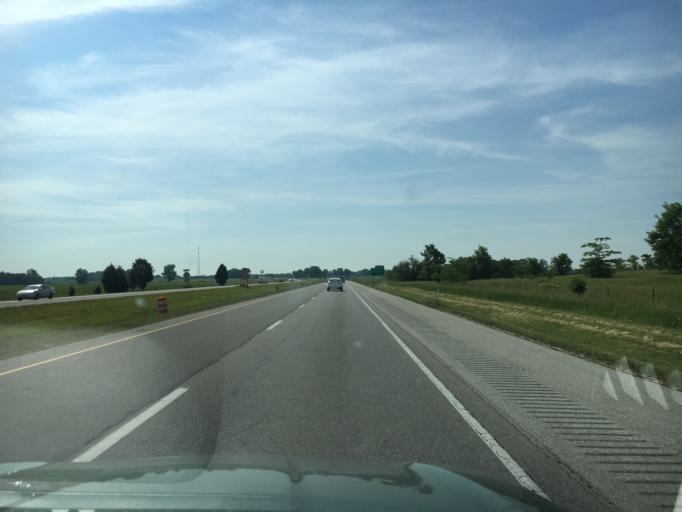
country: US
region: Indiana
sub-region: Decatur County
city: Saint Paul
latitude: 39.4623
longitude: -85.6476
